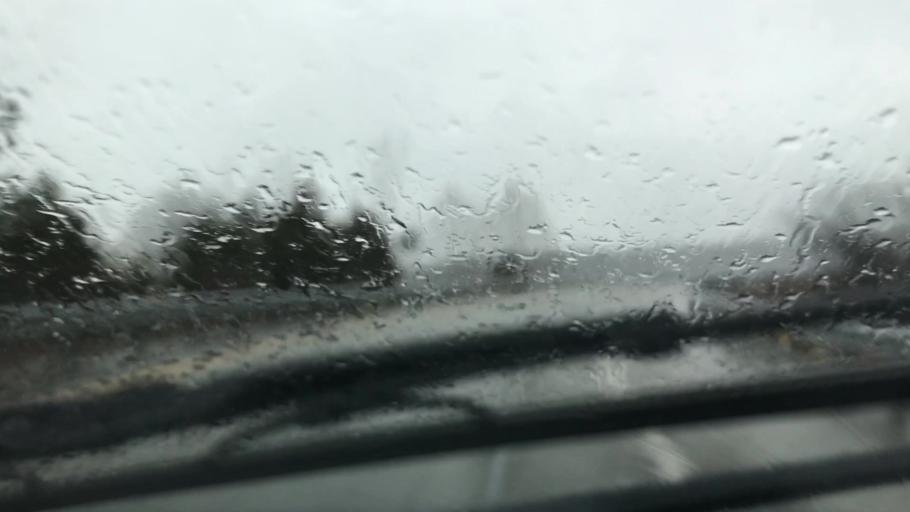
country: US
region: Virginia
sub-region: Henrico County
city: Short Pump
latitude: 37.6624
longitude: -77.6568
